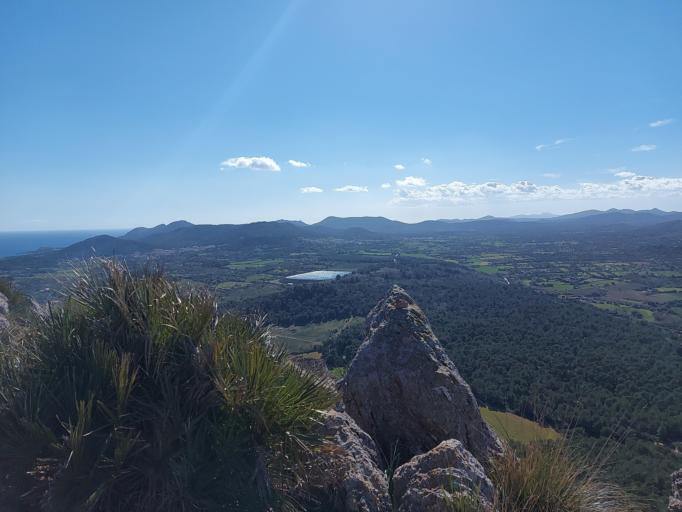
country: ES
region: Balearic Islands
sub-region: Illes Balears
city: Capdepera
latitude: 39.7316
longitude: 3.4368
